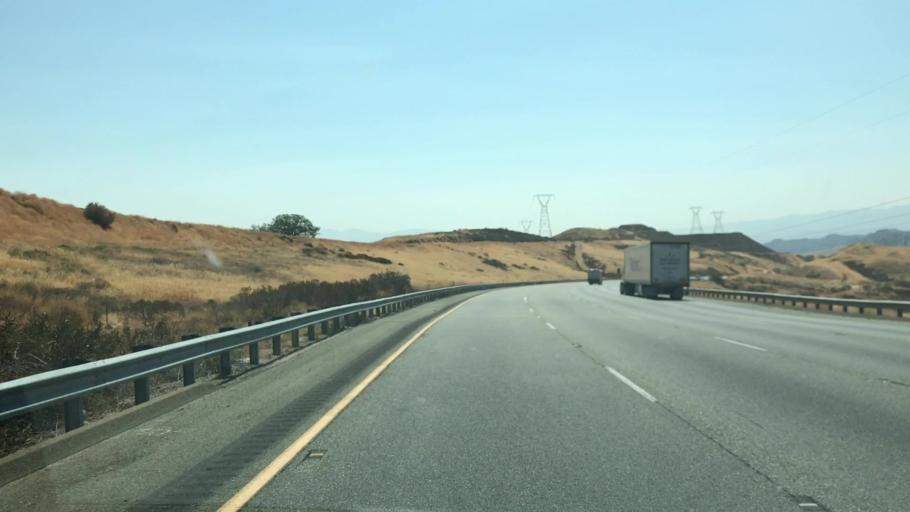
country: US
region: California
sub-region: Los Angeles County
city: Castaic
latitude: 34.5363
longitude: -118.6463
